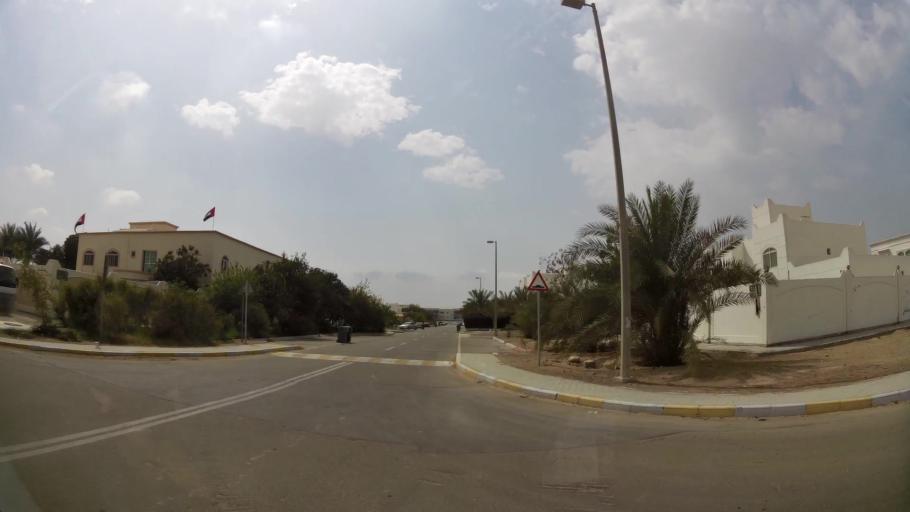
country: AE
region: Abu Dhabi
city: Abu Dhabi
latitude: 24.5414
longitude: 54.6330
